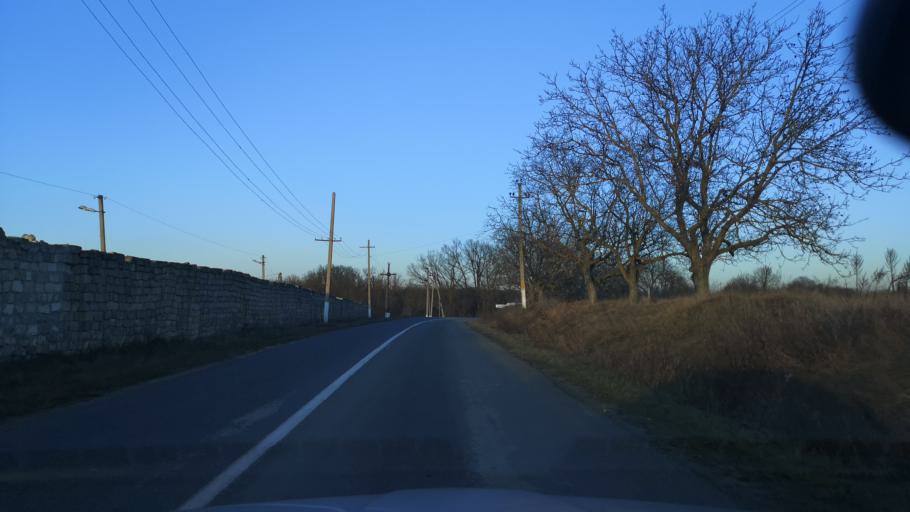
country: MD
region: Orhei
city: Orhei
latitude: 47.3087
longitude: 28.9382
